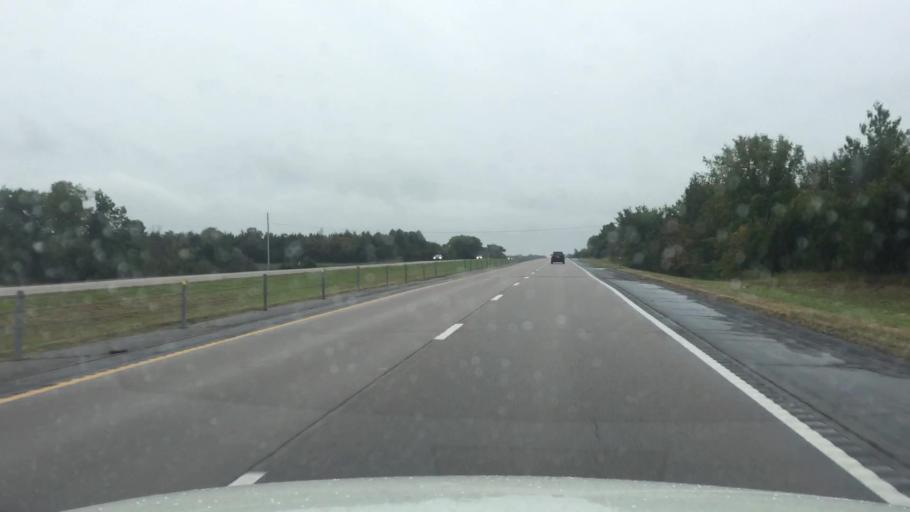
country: US
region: Missouri
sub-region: Boone County
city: Ashland
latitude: 38.7216
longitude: -92.2544
